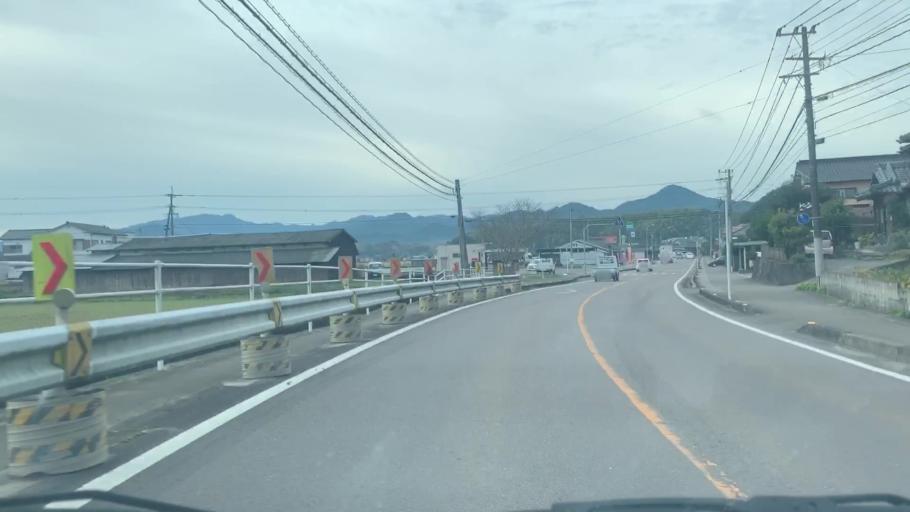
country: JP
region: Saga Prefecture
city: Kashima
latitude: 33.1516
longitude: 130.0648
